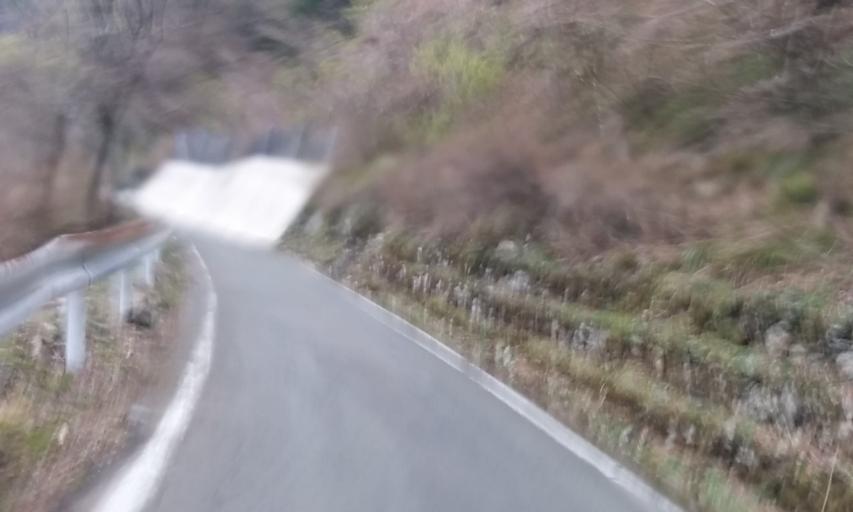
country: JP
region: Ehime
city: Saijo
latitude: 33.7898
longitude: 133.2080
